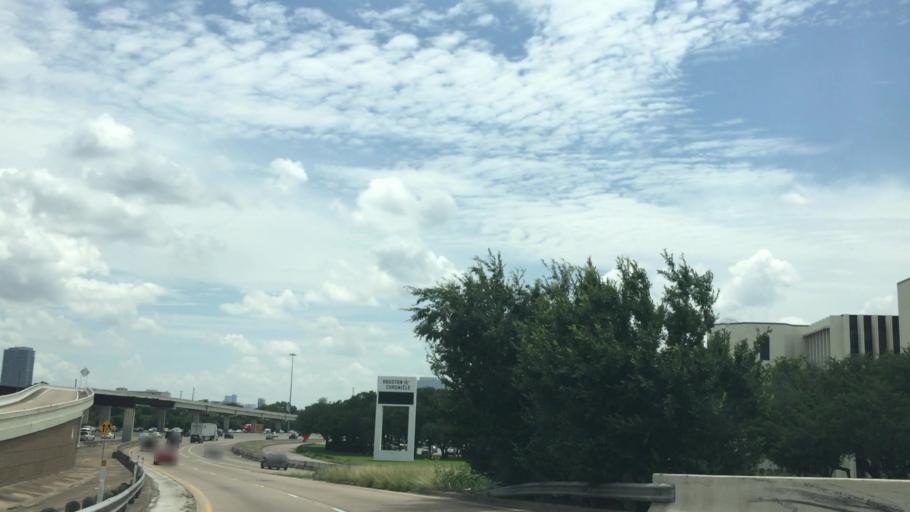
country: US
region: Texas
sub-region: Harris County
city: Bellaire
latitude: 29.7285
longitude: -95.4583
